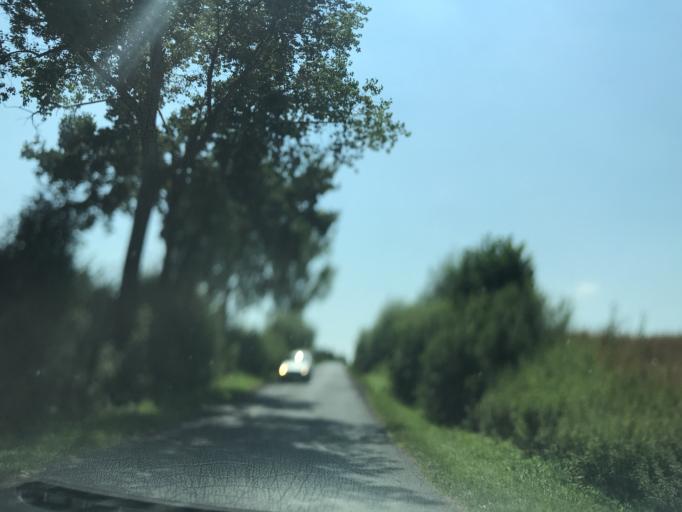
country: PL
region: Kujawsko-Pomorskie
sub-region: Powiat golubsko-dobrzynski
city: Zbojno
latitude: 52.9807
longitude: 19.2056
